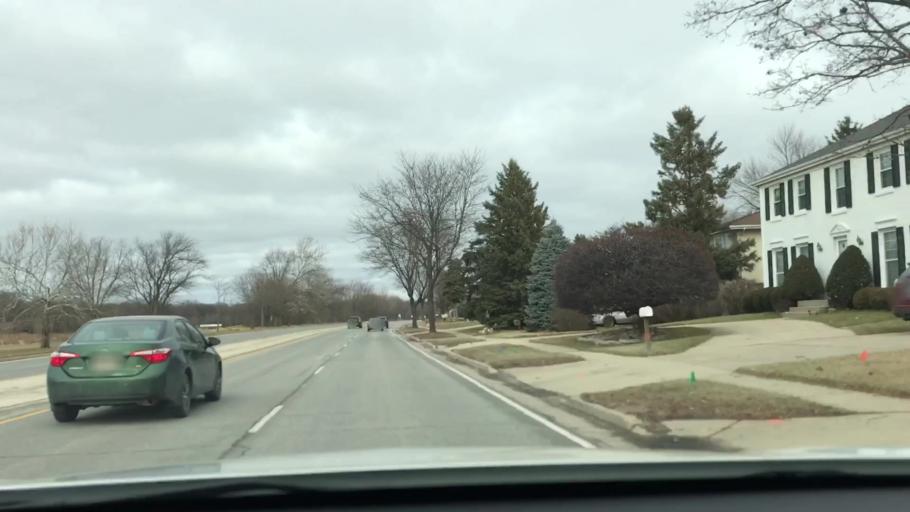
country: US
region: Illinois
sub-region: Cook County
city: Elk Grove Village
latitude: 42.0235
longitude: -87.9883
